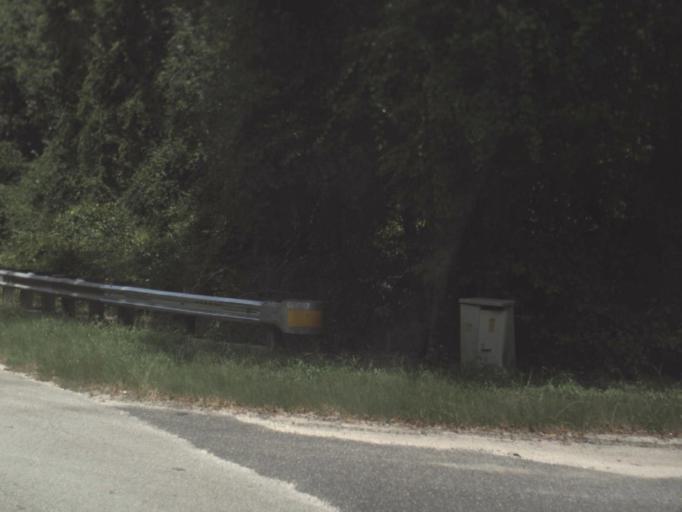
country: US
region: Florida
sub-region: Alachua County
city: High Springs
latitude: 29.8125
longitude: -82.6055
